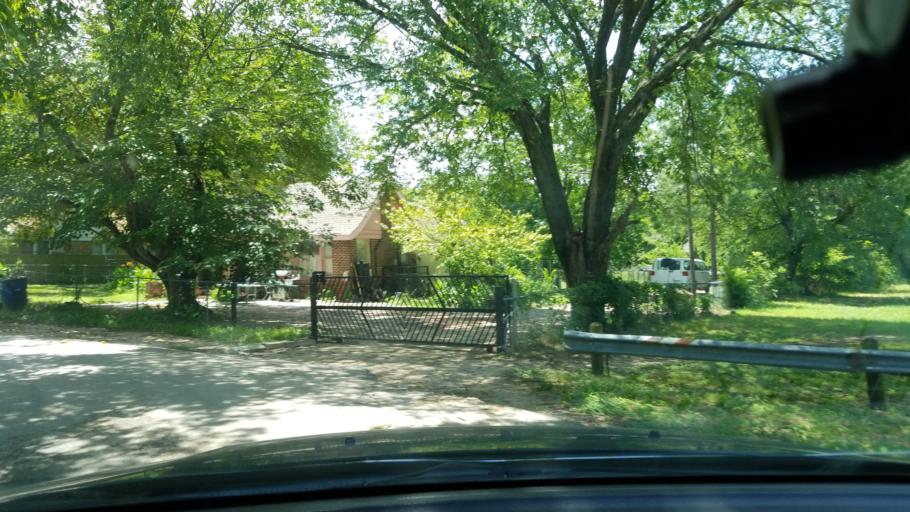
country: US
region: Texas
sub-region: Dallas County
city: Balch Springs
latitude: 32.7515
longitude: -96.6504
